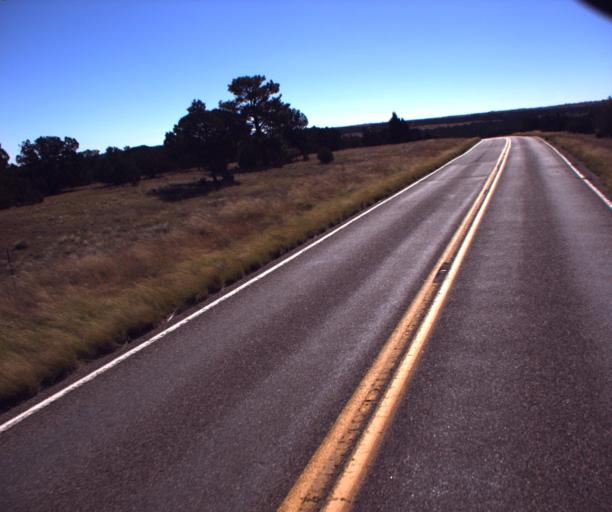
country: US
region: Arizona
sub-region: Navajo County
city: Heber-Overgaard
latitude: 34.4566
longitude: -110.4648
